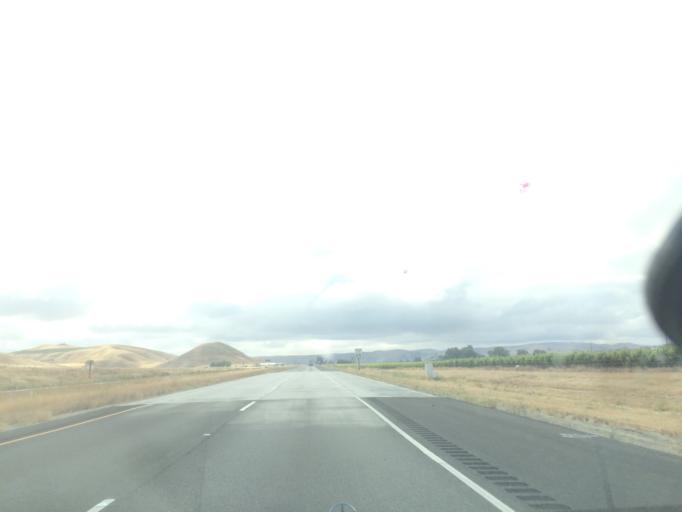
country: US
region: California
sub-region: San Luis Obispo County
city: Shandon
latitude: 35.6614
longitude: -120.4285
